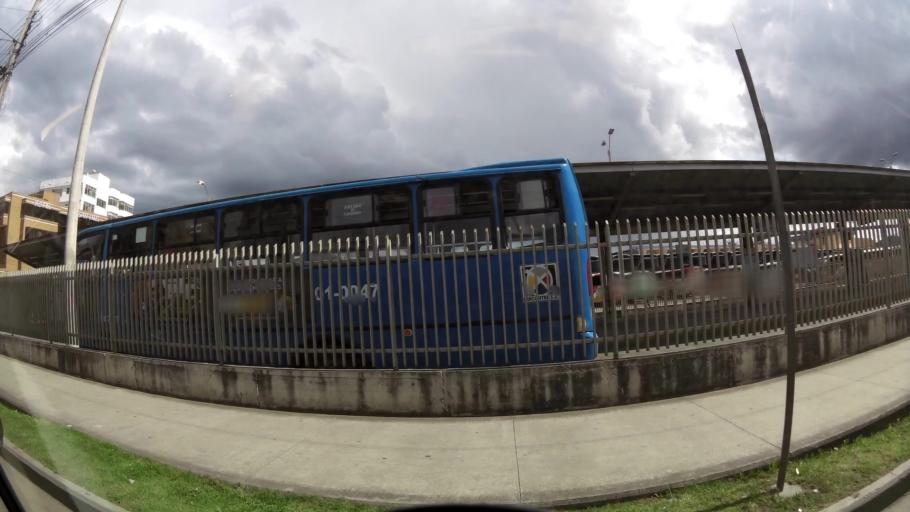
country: EC
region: Azuay
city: Cuenca
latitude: -2.8911
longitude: -78.9924
